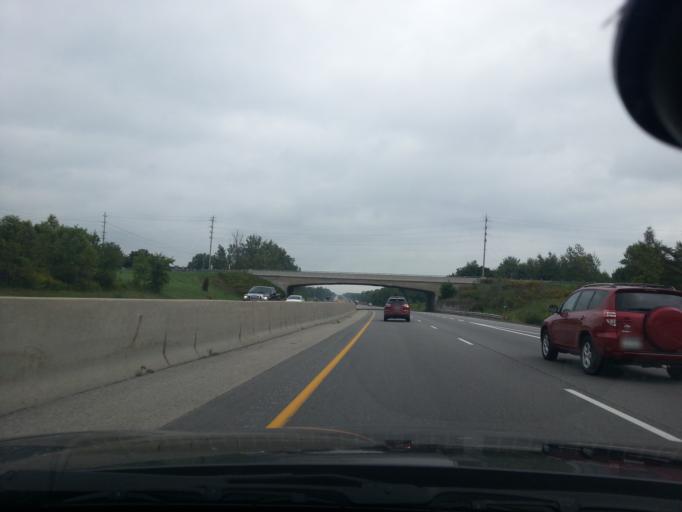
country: CA
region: Ontario
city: Brockville
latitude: 44.6520
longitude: -75.6270
